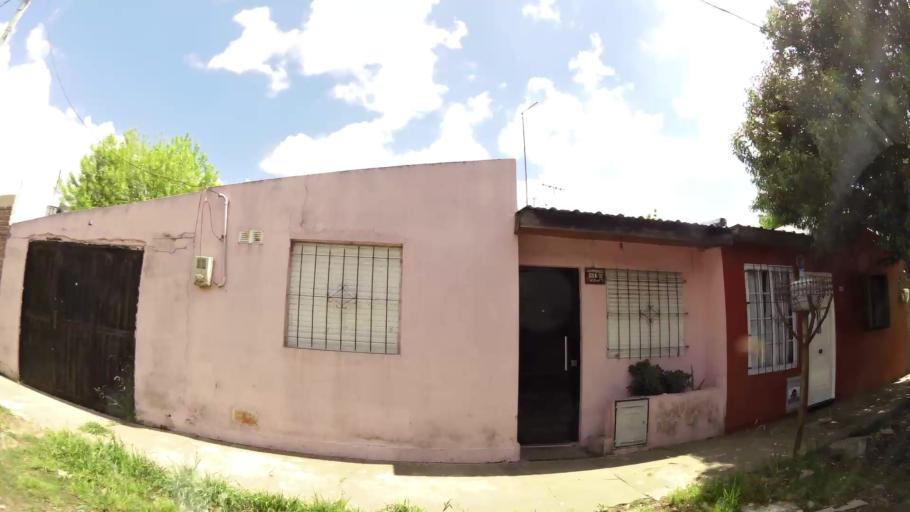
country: AR
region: Buenos Aires
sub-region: Partido de Quilmes
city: Quilmes
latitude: -34.8362
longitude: -58.2375
